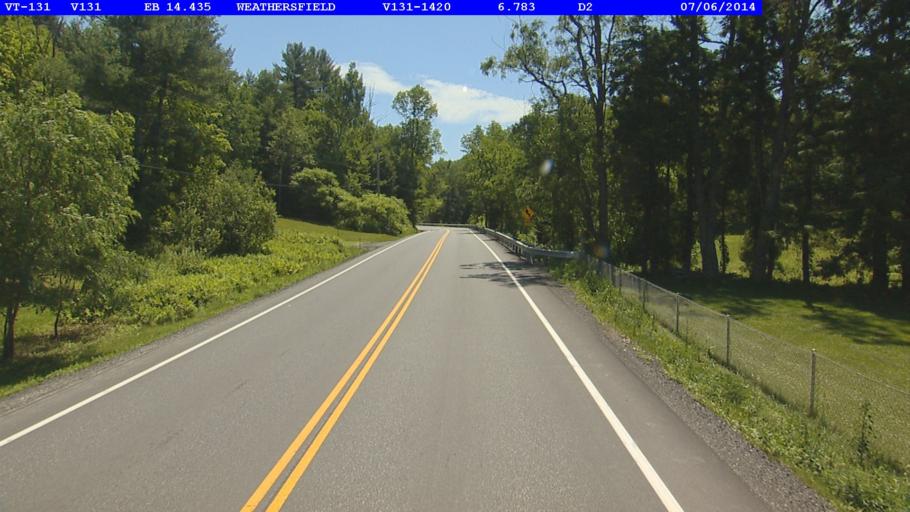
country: US
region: Vermont
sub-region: Windsor County
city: Windsor
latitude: 43.4078
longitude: -72.4394
